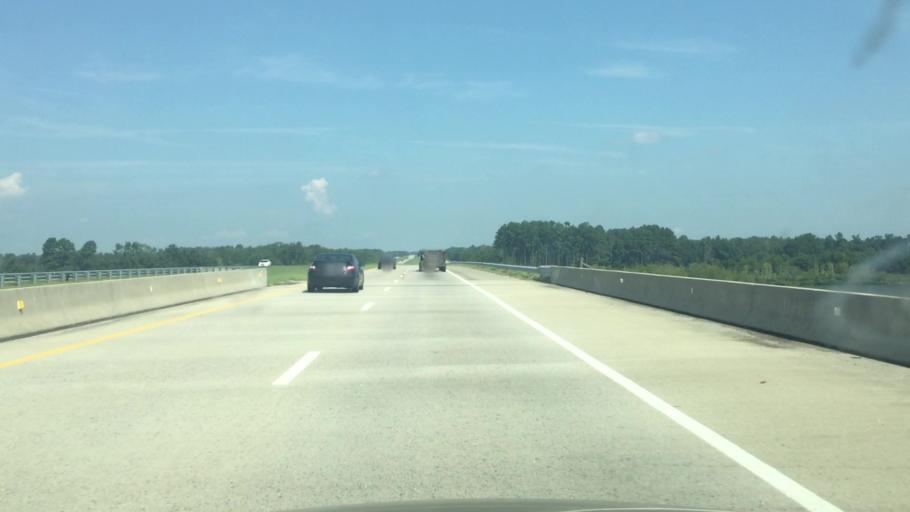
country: US
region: North Carolina
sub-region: Robeson County
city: Pembroke
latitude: 34.6330
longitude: -79.2279
